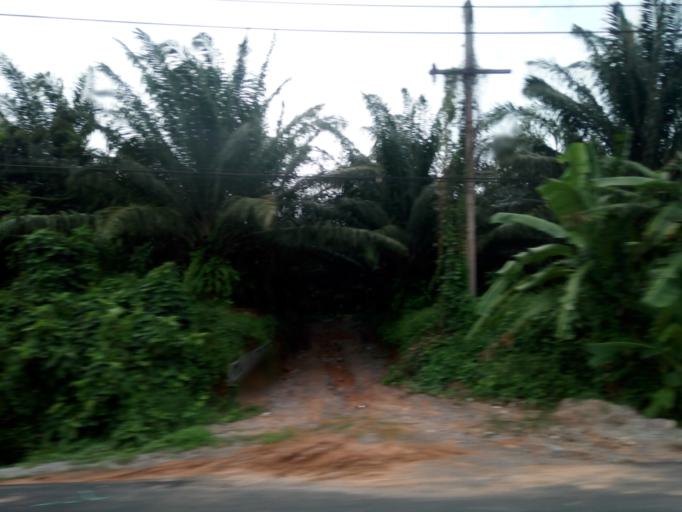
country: TH
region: Phuket
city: Ban Ko Kaeo
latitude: 7.9461
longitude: 98.3846
